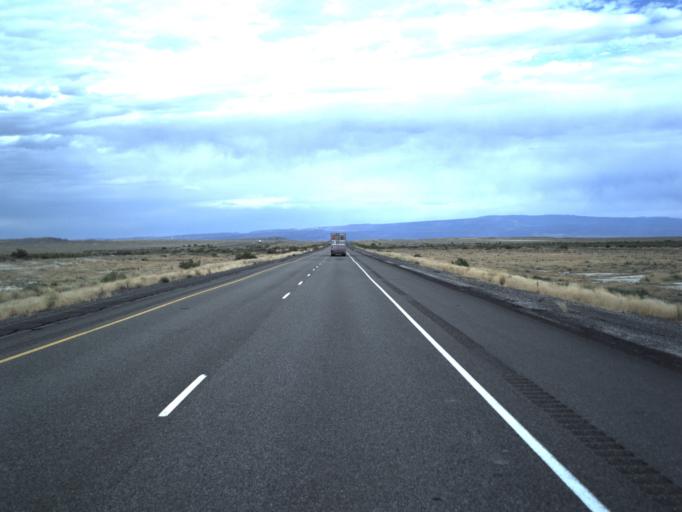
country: US
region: Utah
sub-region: Grand County
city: Moab
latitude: 38.9418
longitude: -109.5672
